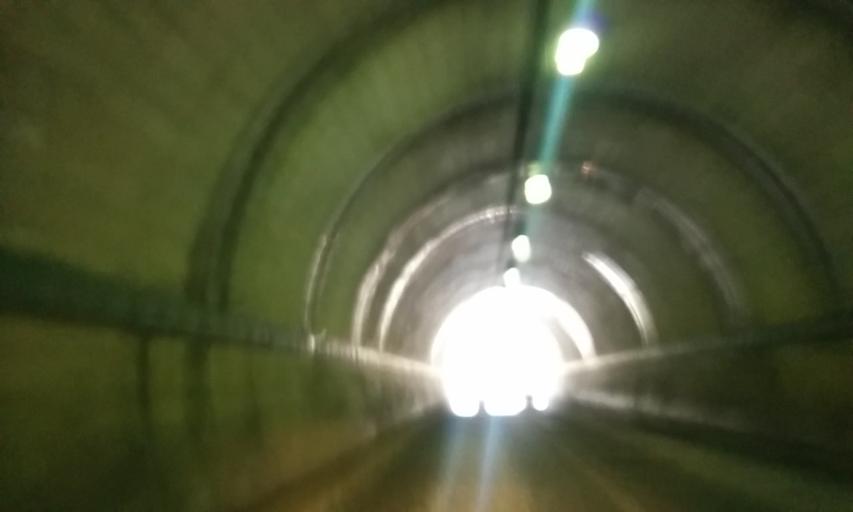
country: JP
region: Gifu
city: Takayama
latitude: 36.1798
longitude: 137.4790
